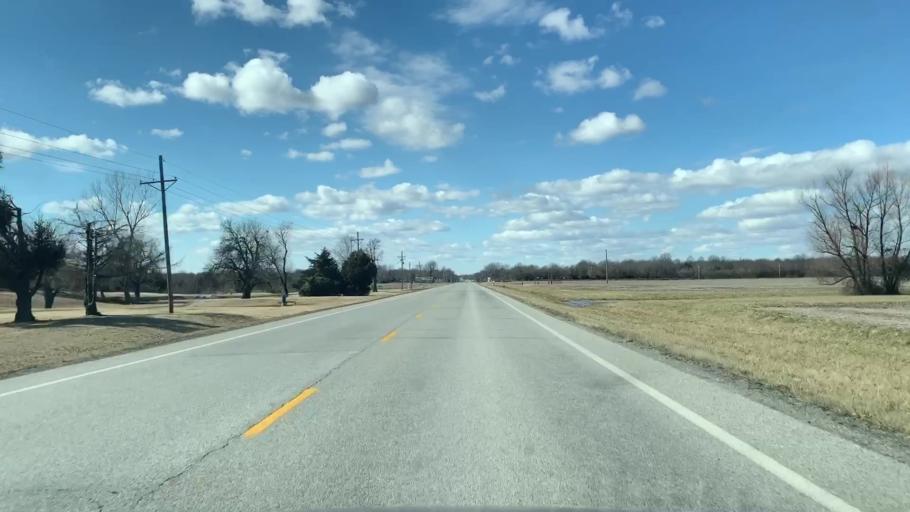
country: US
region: Kansas
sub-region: Cherokee County
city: Columbus
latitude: 37.1781
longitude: -94.8067
